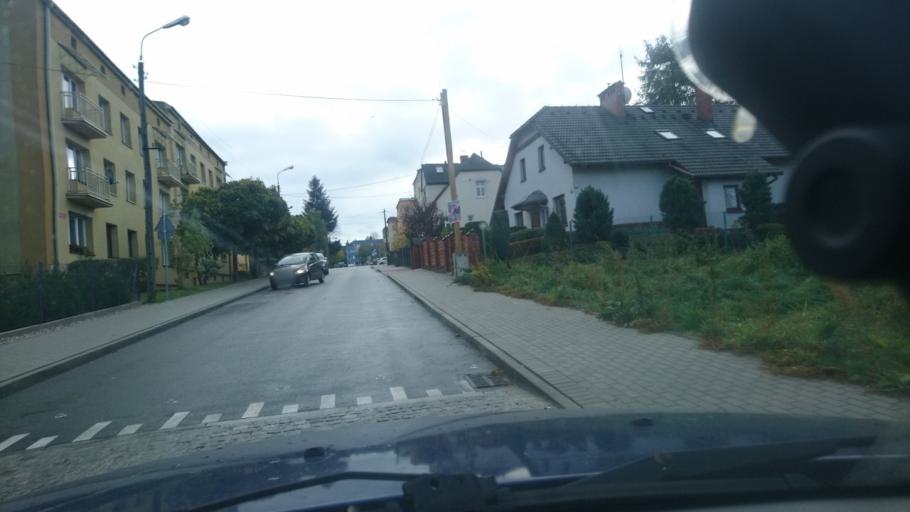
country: PL
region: Silesian Voivodeship
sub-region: Bielsko-Biala
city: Bielsko-Biala
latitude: 49.8267
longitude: 19.0272
